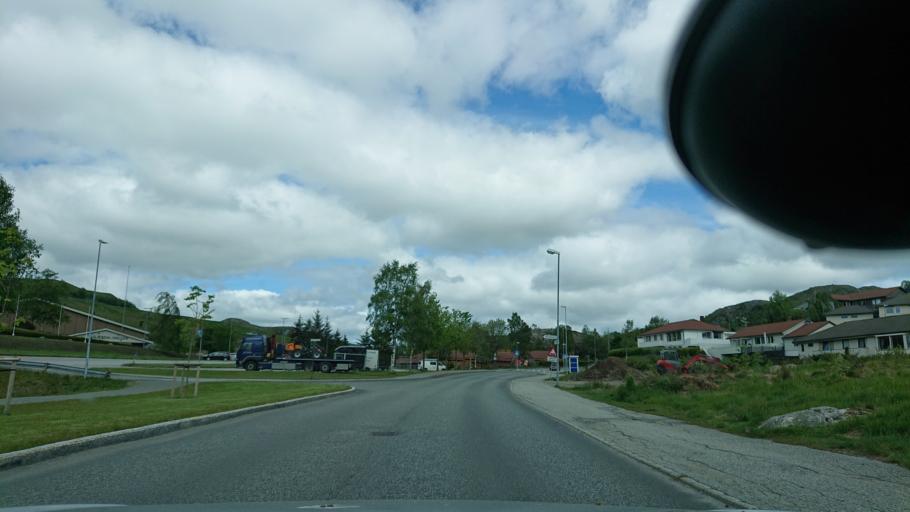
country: NO
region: Rogaland
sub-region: Gjesdal
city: Algard
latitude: 58.7716
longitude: 5.8650
